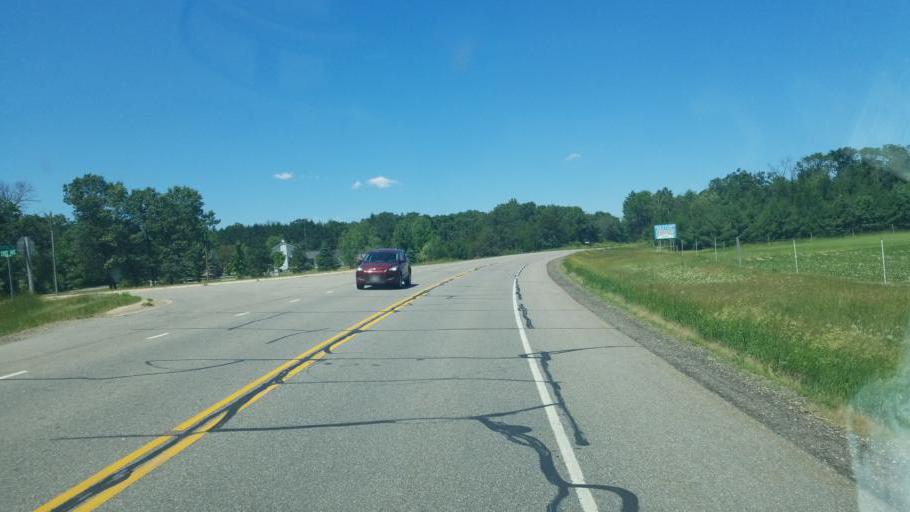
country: US
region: Wisconsin
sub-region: Adams County
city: Friendship
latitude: 44.0399
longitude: -89.9579
